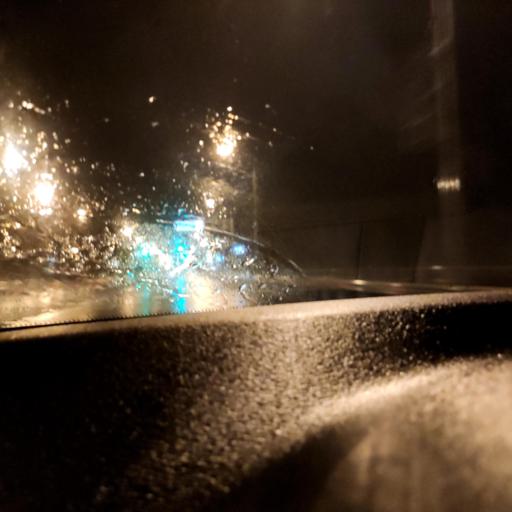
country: RU
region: Samara
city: Petra-Dubrava
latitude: 53.3038
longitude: 50.2407
